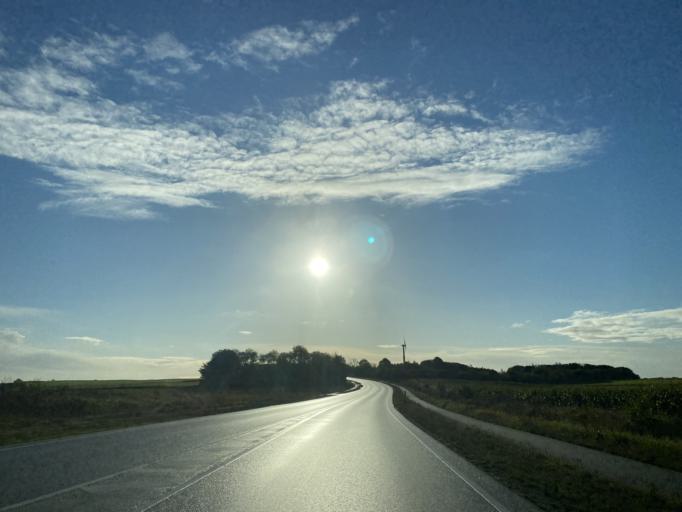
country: DK
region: Central Jutland
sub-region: Horsens Kommune
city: Braedstrup
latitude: 55.9179
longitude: 9.6975
